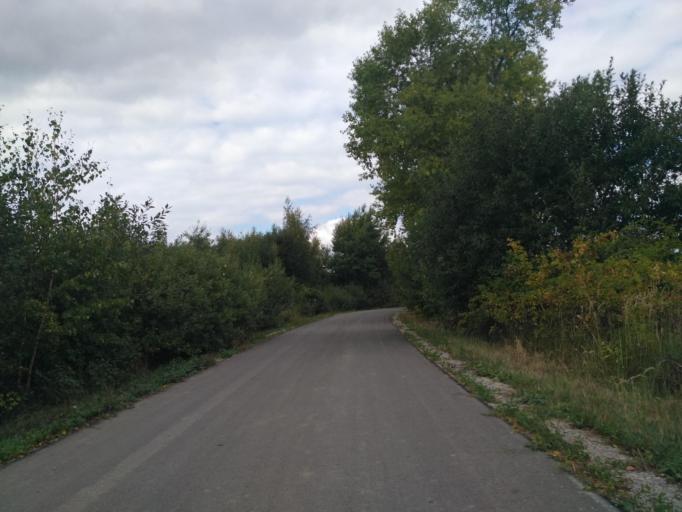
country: PL
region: Subcarpathian Voivodeship
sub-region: Powiat rzeszowski
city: Dynow
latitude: 49.7741
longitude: 22.2803
